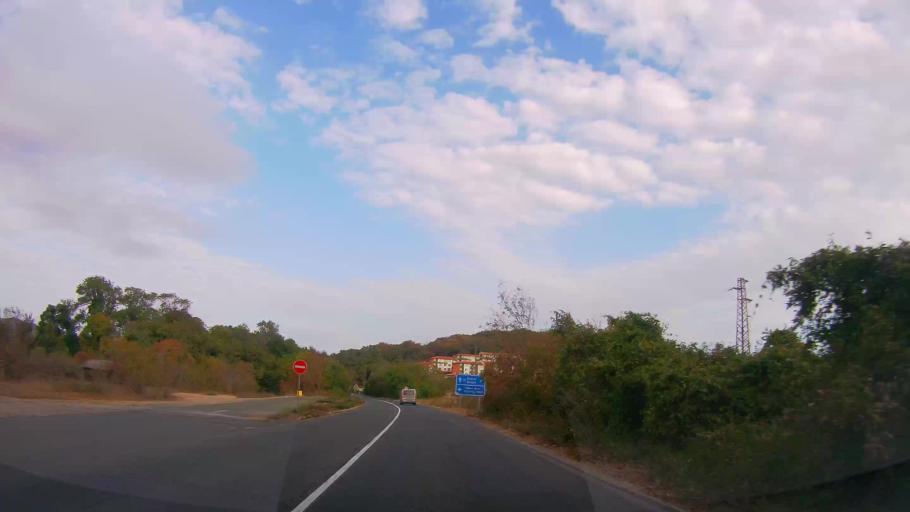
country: BG
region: Burgas
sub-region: Obshtina Primorsko
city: Primorsko
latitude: 42.3314
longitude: 27.7284
